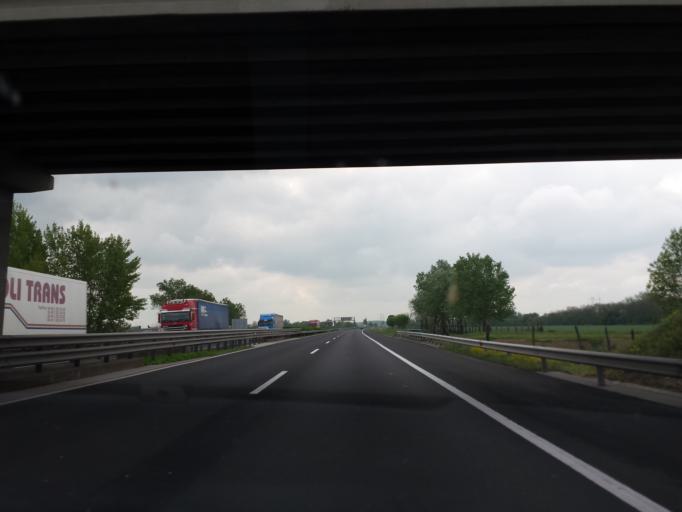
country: HU
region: Gyor-Moson-Sopron
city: Mosonmagyarovar
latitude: 47.8342
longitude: 17.2720
